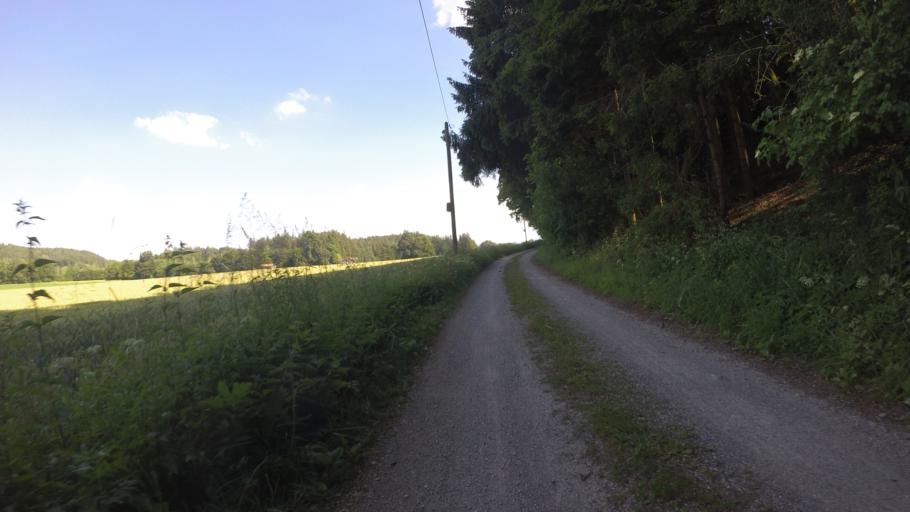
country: DE
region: Bavaria
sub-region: Upper Bavaria
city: Seeon-Seebruck
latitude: 47.9682
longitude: 12.5044
